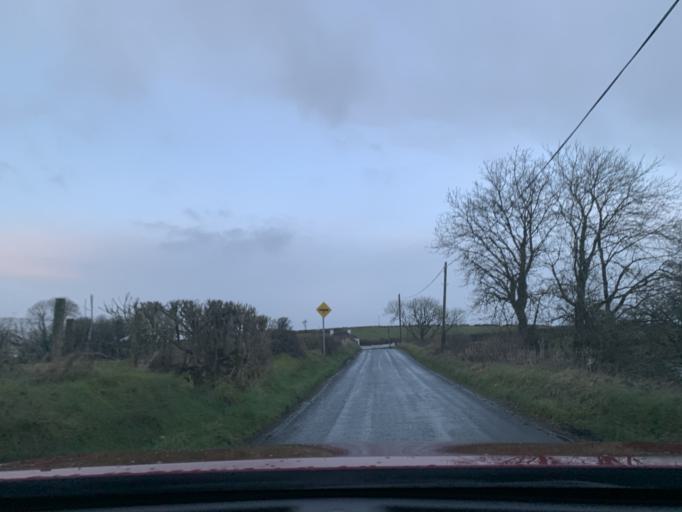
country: IE
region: Connaught
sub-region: Sligo
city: Ballymote
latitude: 54.0455
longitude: -8.6080
